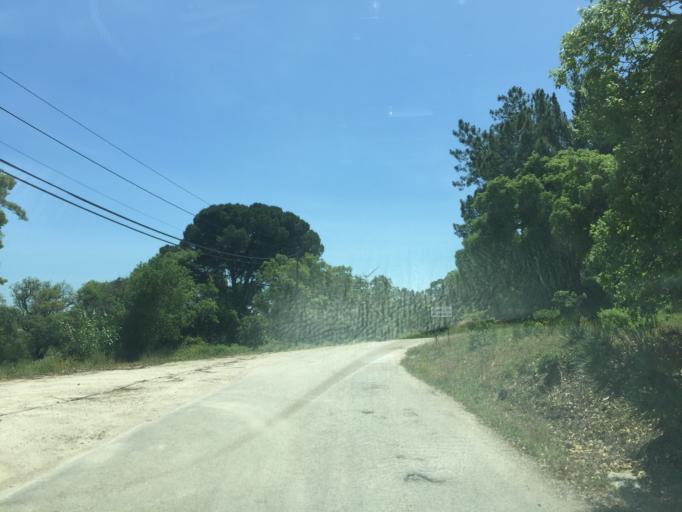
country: PT
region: Lisbon
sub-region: Mafra
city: Venda do Pinheiro
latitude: 38.8914
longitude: -9.2273
